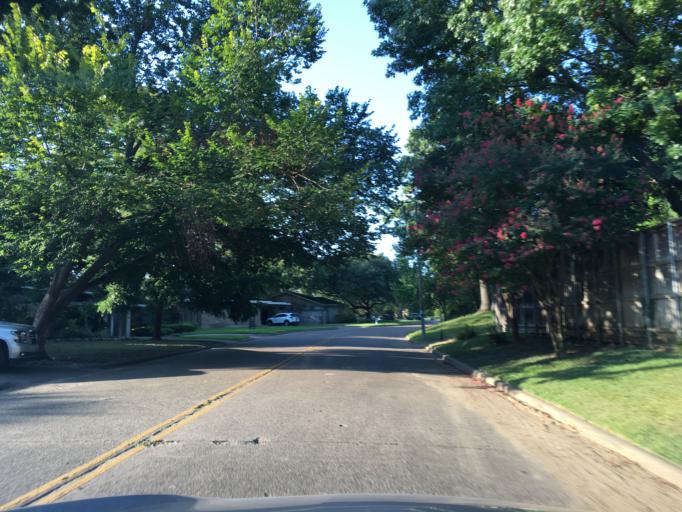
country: US
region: Texas
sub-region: Dallas County
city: Highland Park
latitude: 32.8587
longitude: -96.7343
